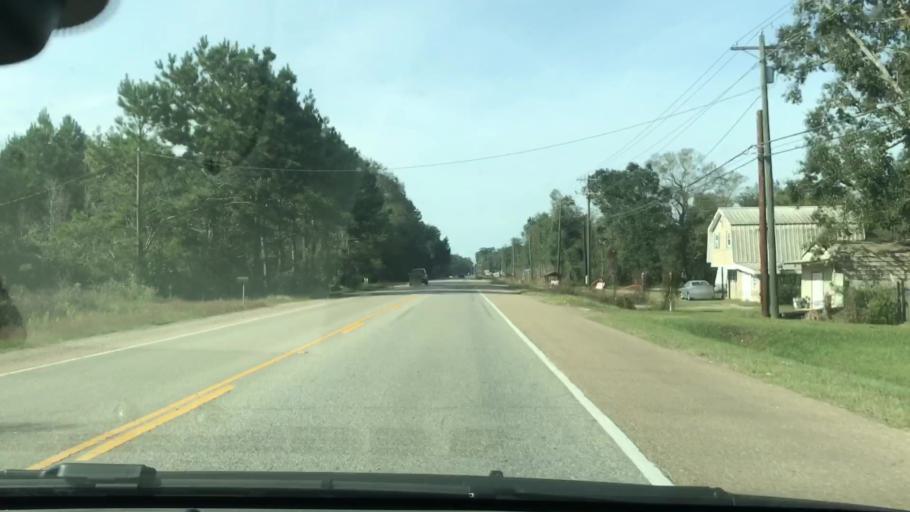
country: US
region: Louisiana
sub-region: Saint Tammany Parish
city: Pearl River
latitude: 30.4084
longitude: -89.7745
